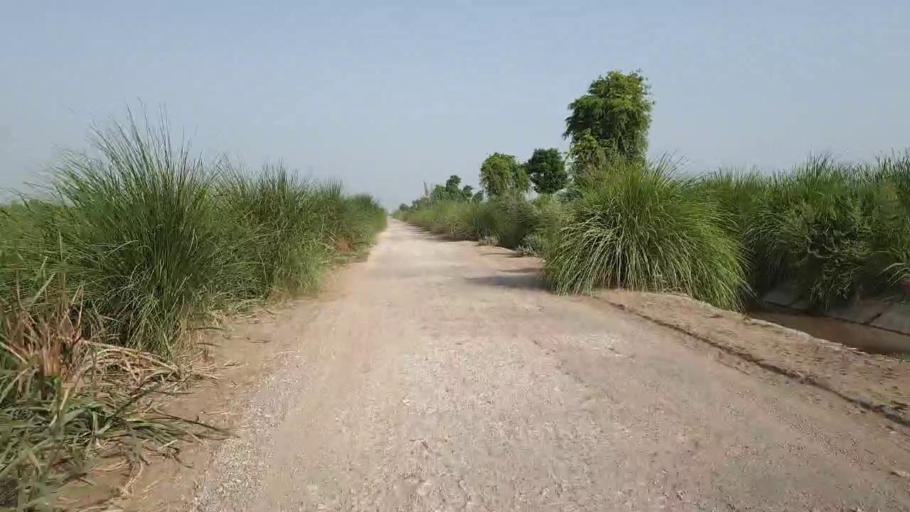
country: PK
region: Sindh
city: Daur
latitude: 26.3456
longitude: 68.1779
